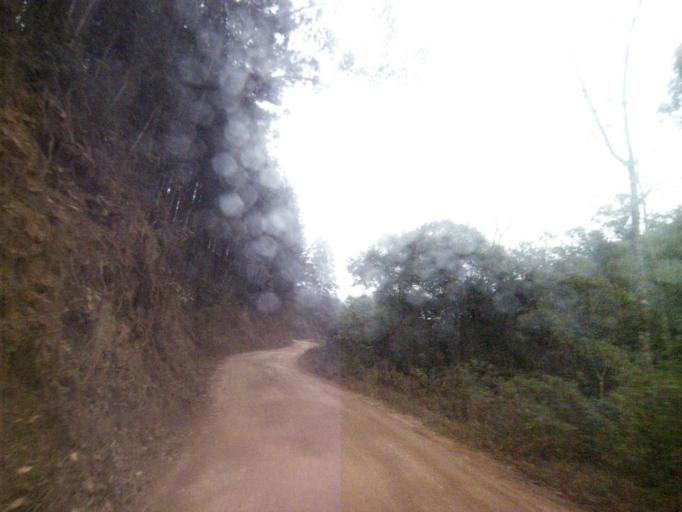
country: BR
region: Santa Catarina
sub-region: Anitapolis
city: Anitapolis
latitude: -27.8939
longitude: -49.1296
